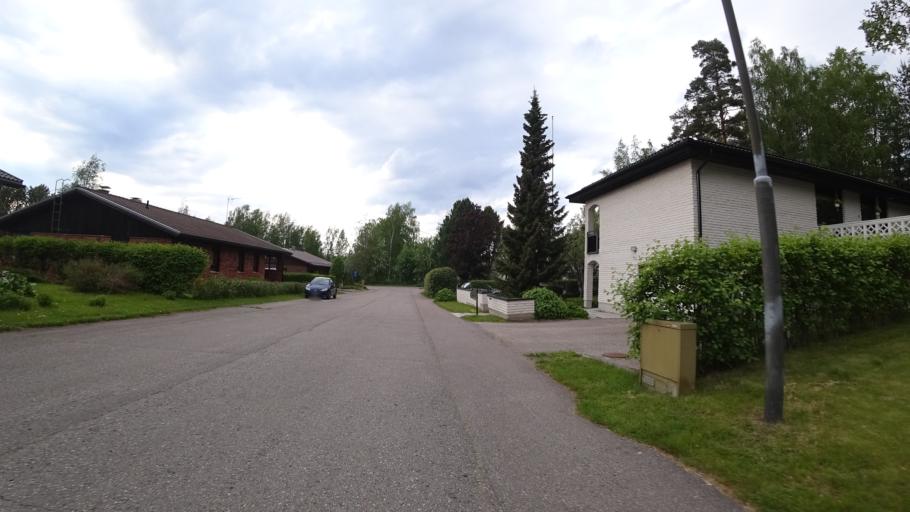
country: FI
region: Pirkanmaa
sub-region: Tampere
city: Yloejaervi
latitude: 61.5222
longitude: 23.6078
